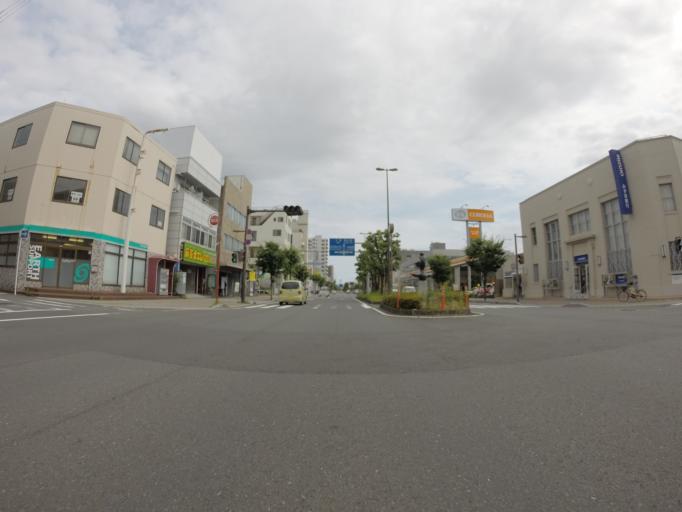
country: JP
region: Shizuoka
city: Shizuoka-shi
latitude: 35.0163
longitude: 138.4883
